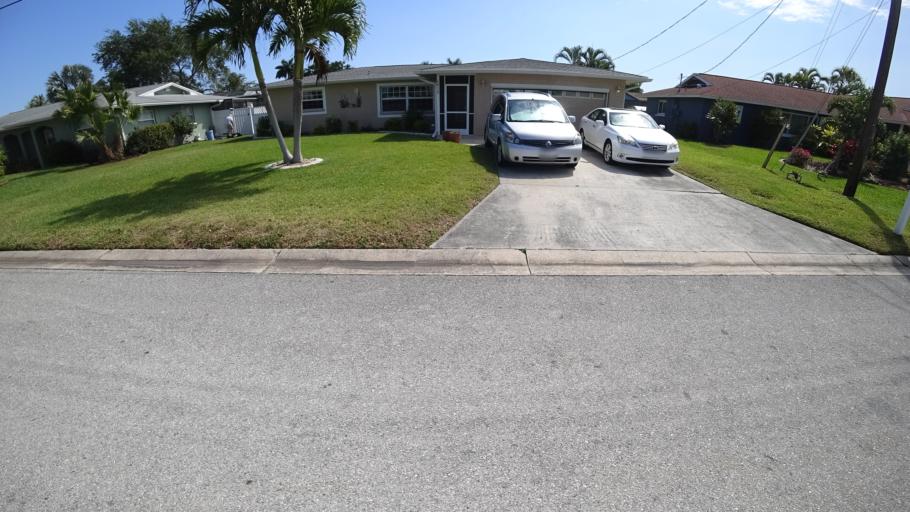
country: US
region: Florida
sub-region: Manatee County
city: Cortez
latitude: 27.4561
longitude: -82.6539
